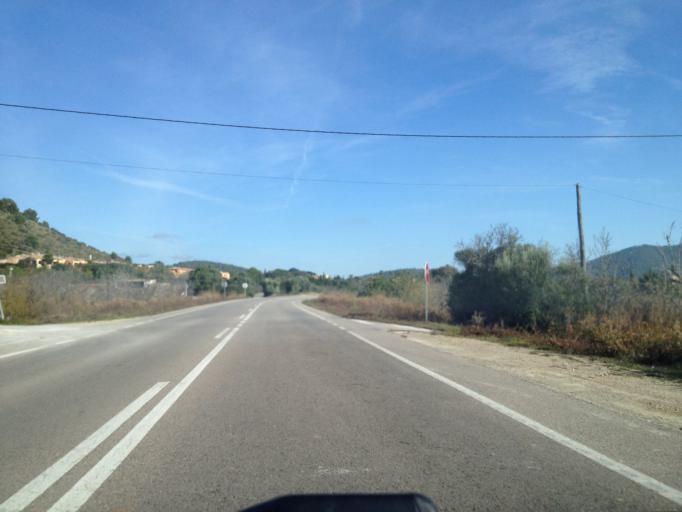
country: ES
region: Balearic Islands
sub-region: Illes Balears
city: Son Servera
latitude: 39.6417
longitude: 3.3725
